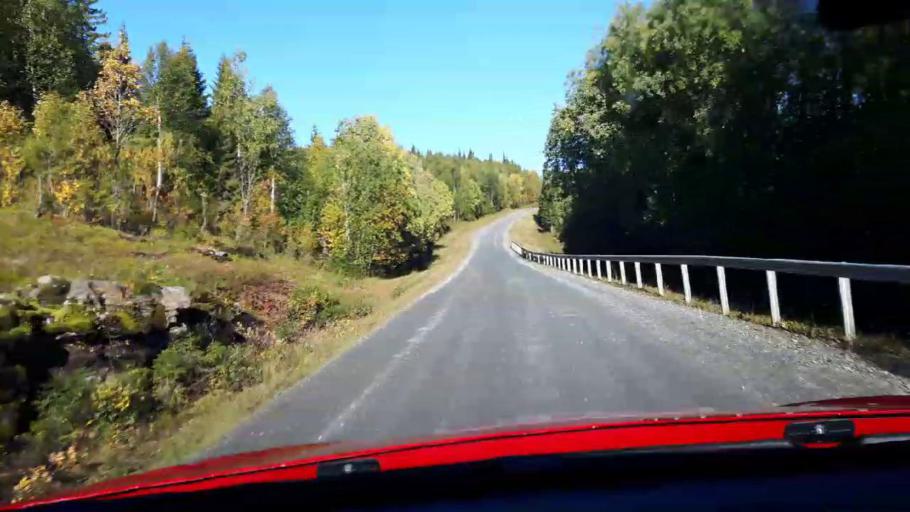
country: NO
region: Nord-Trondelag
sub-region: Lierne
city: Sandvika
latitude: 64.5785
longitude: 13.8942
